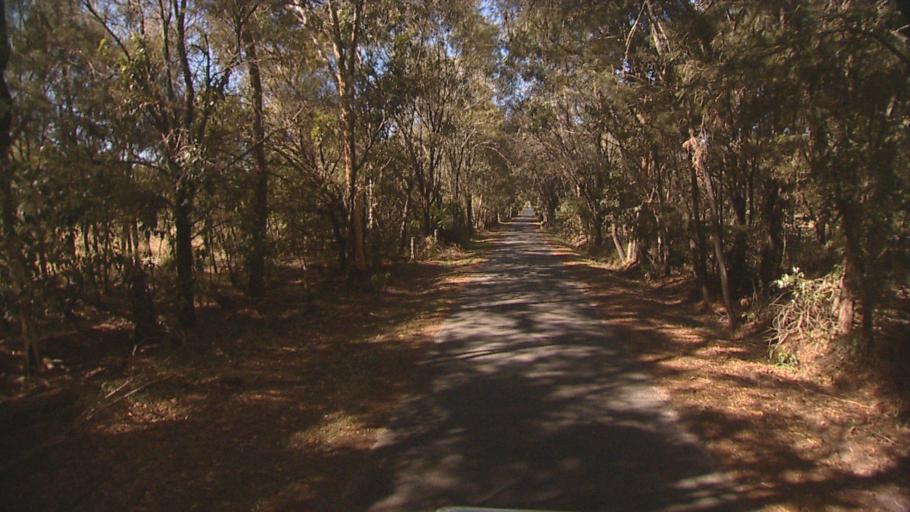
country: AU
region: Queensland
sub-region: Logan
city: Logan Reserve
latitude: -27.7154
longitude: 153.0734
